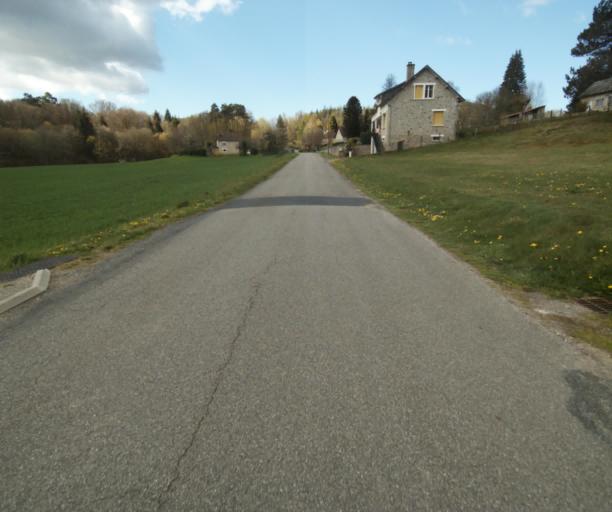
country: FR
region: Limousin
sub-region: Departement de la Correze
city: Laguenne
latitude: 45.2268
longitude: 1.8962
